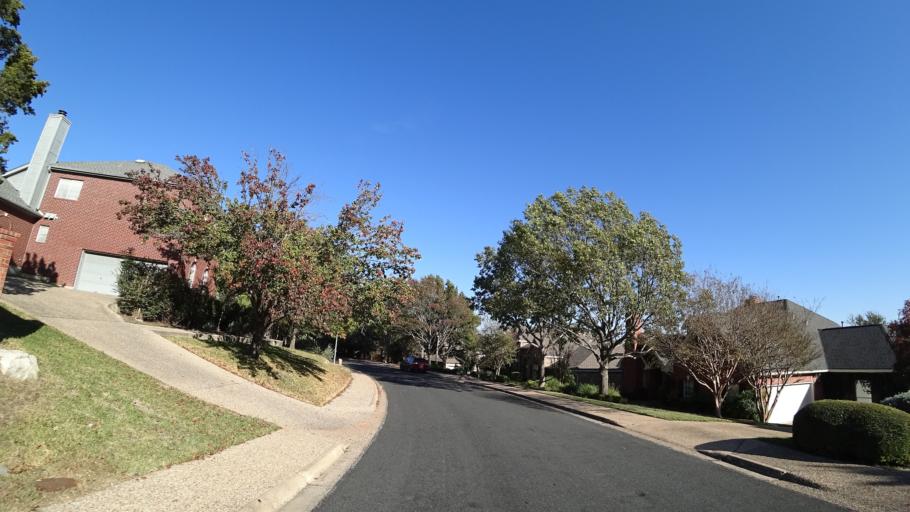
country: US
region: Texas
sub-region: Williamson County
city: Jollyville
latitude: 30.4134
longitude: -97.7758
